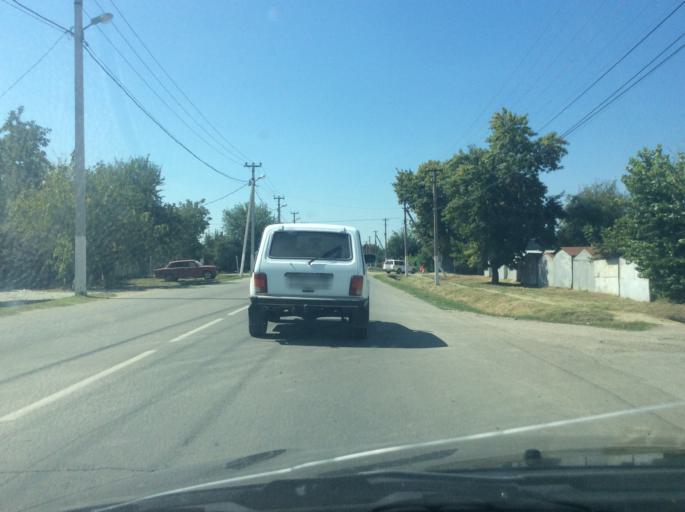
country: RU
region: Krasnodarskiy
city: Slavyansk-na-Kubani
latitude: 45.2510
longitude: 38.1096
